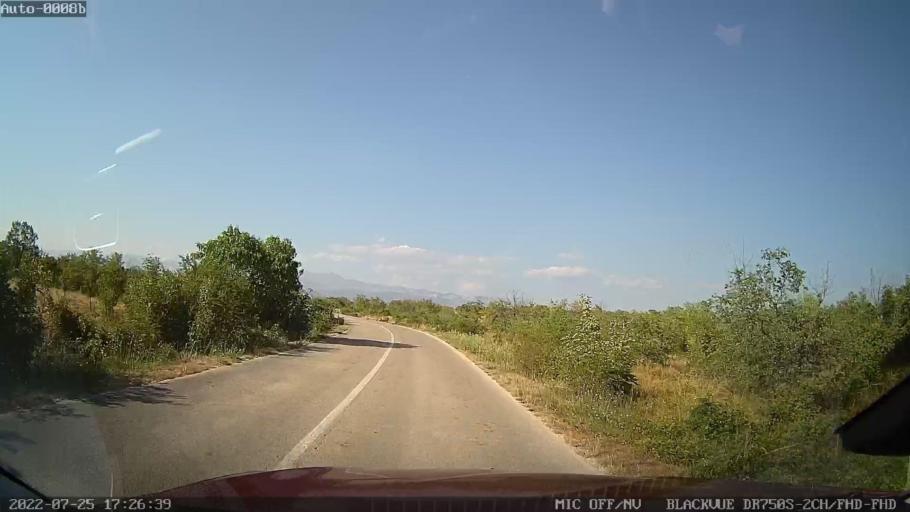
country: HR
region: Zadarska
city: Pridraga
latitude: 44.1355
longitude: 15.5018
